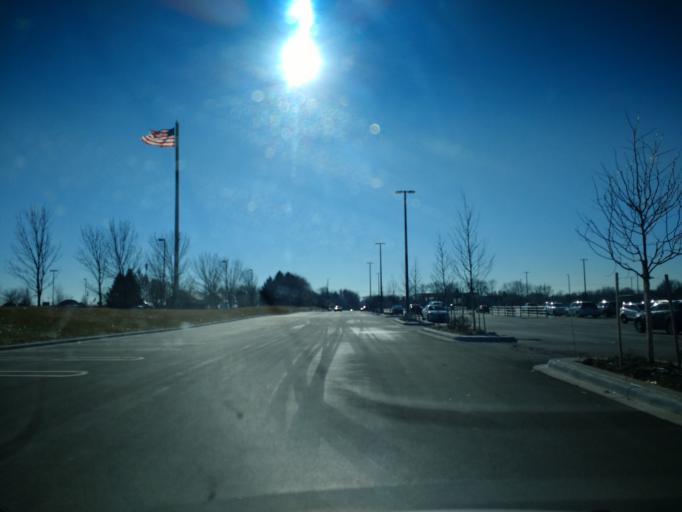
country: US
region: Iowa
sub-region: Scott County
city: Bettendorf
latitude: 41.5771
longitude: -90.5329
